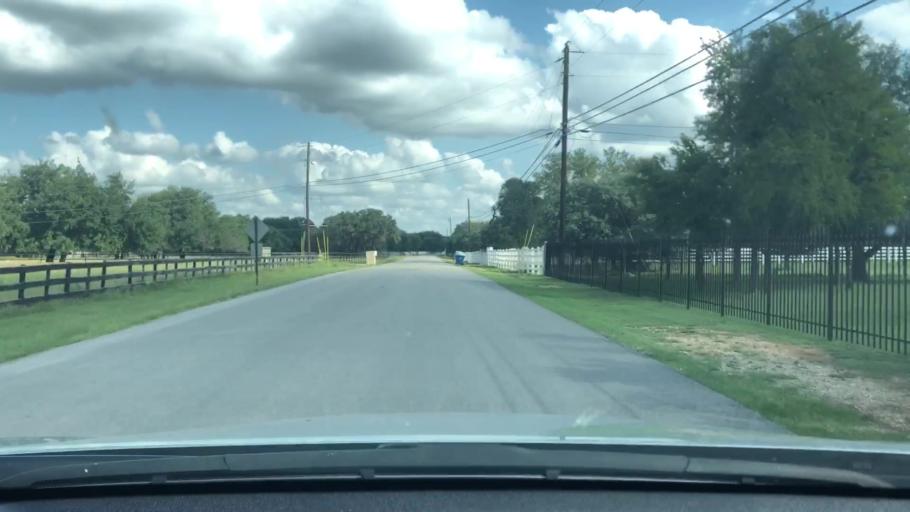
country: US
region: Texas
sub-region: Bexar County
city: Fair Oaks Ranch
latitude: 29.7633
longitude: -98.6296
